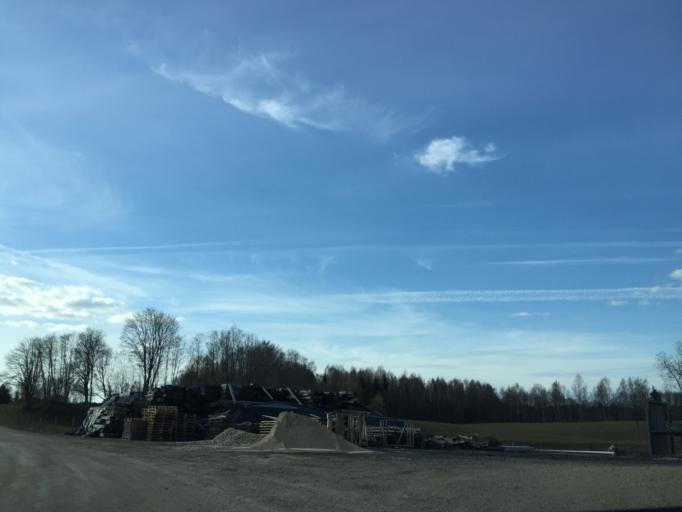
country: EE
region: Tartu
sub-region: Noo vald
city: Noo
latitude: 58.1319
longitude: 26.5905
